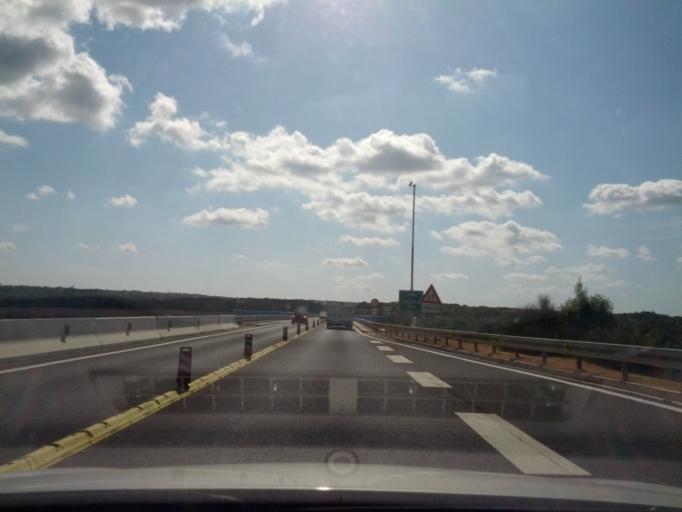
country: HR
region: Istarska
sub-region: Grad Rovinj
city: Rovinj
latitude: 45.1220
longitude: 13.7965
